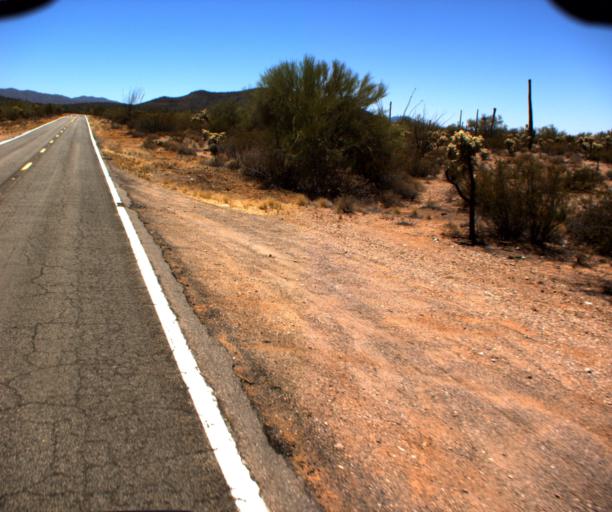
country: US
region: Arizona
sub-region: Pima County
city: Sells
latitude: 32.1801
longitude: -112.2771
